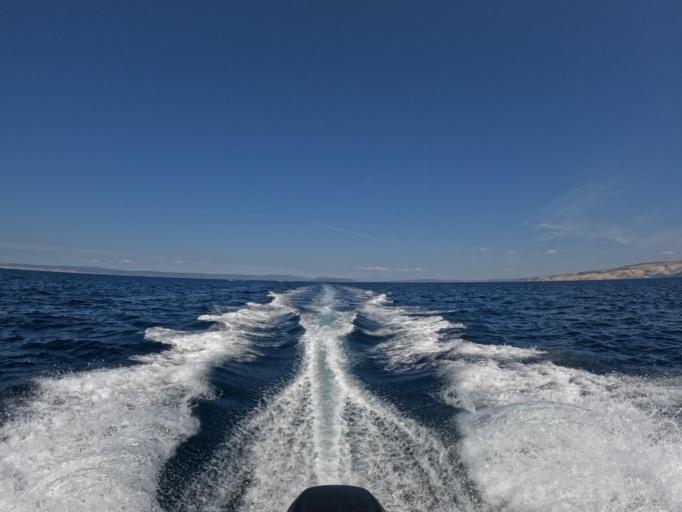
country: HR
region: Primorsko-Goranska
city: Lopar
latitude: 44.8862
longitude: 14.6506
